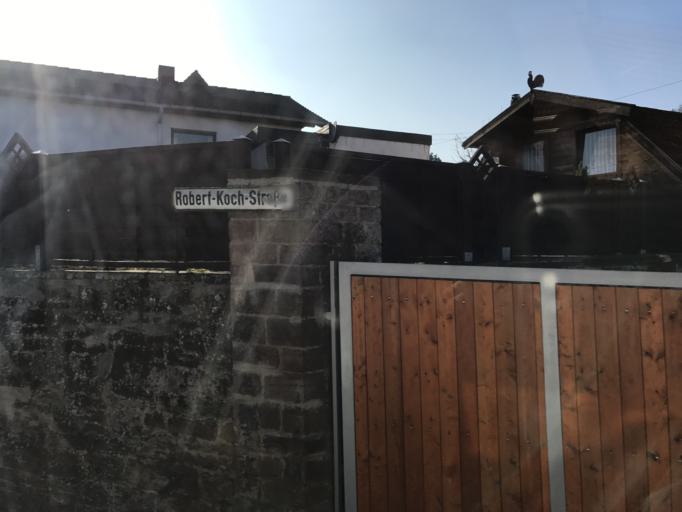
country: DE
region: Rheinland-Pfalz
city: Obermoschel
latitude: 49.7273
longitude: 7.7697
